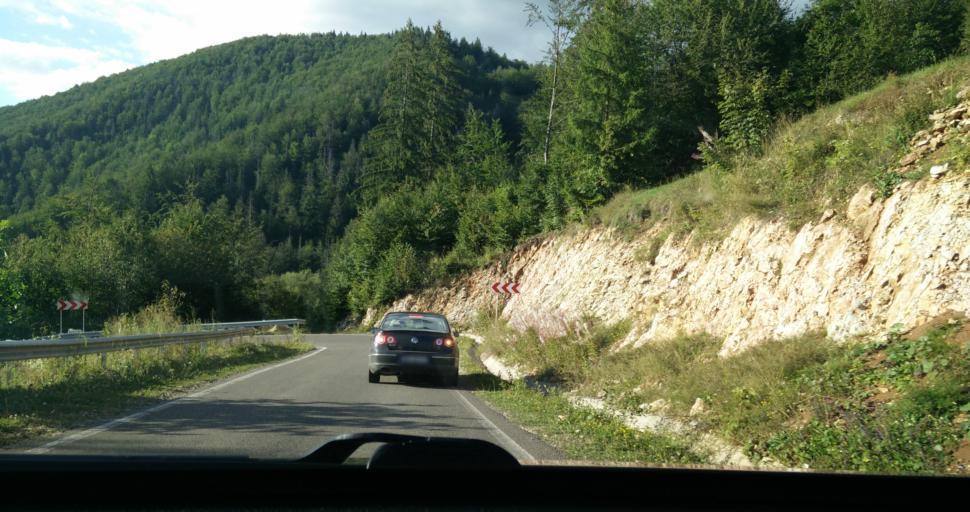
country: RO
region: Alba
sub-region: Comuna Scarisoara
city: Scarisoara
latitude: 46.4689
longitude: 22.8281
